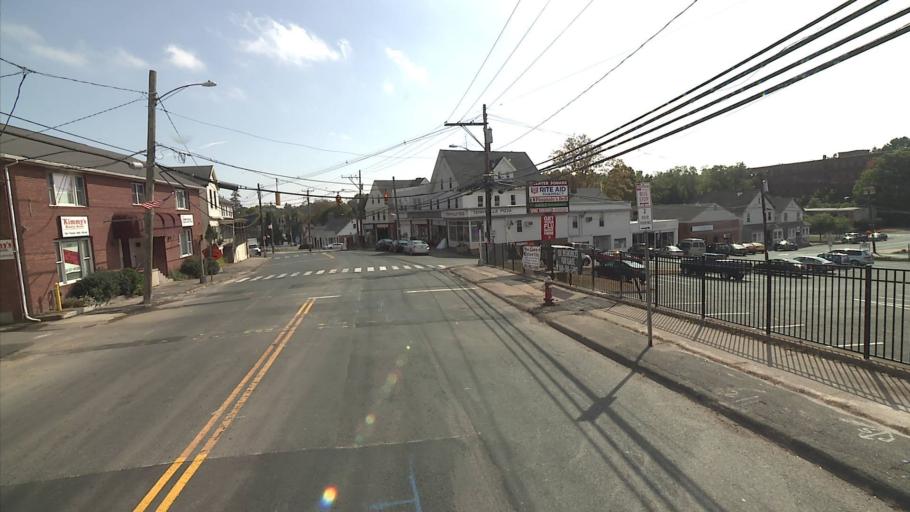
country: US
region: Connecticut
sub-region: Litchfield County
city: Terryville
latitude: 41.6786
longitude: -73.0116
